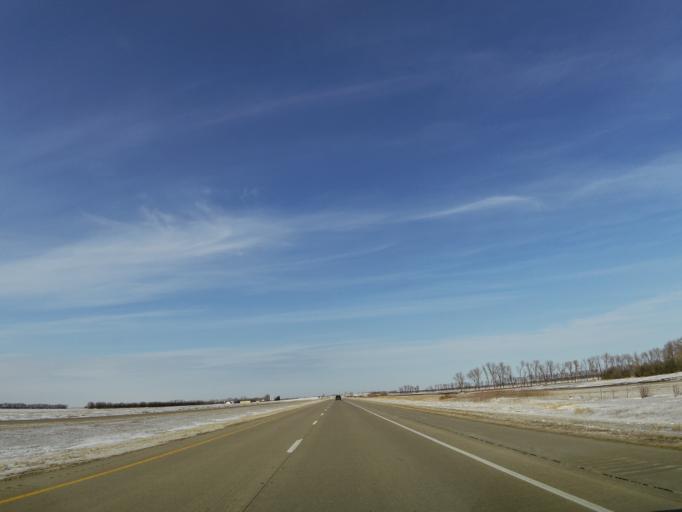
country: US
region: North Dakota
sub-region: Walsh County
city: Grafton
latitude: 48.4277
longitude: -97.1904
